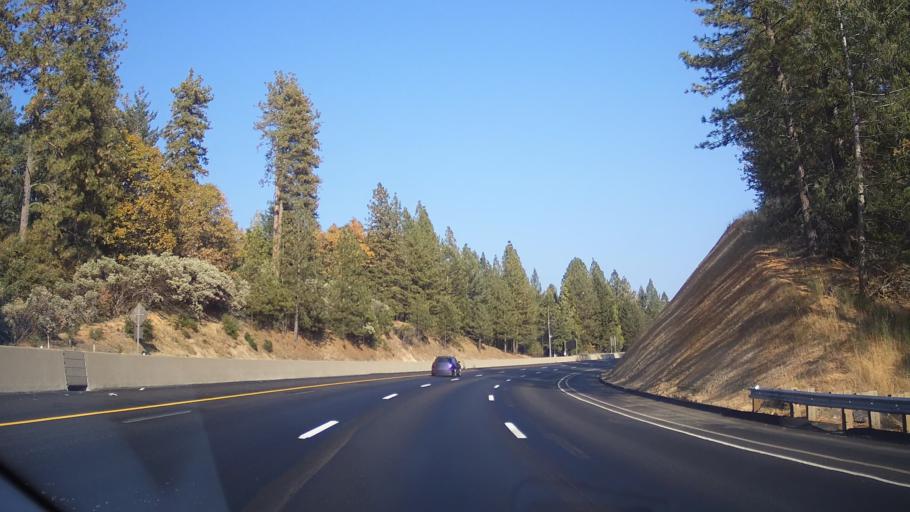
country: US
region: California
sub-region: Placer County
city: Colfax
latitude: 39.1383
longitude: -120.9285
